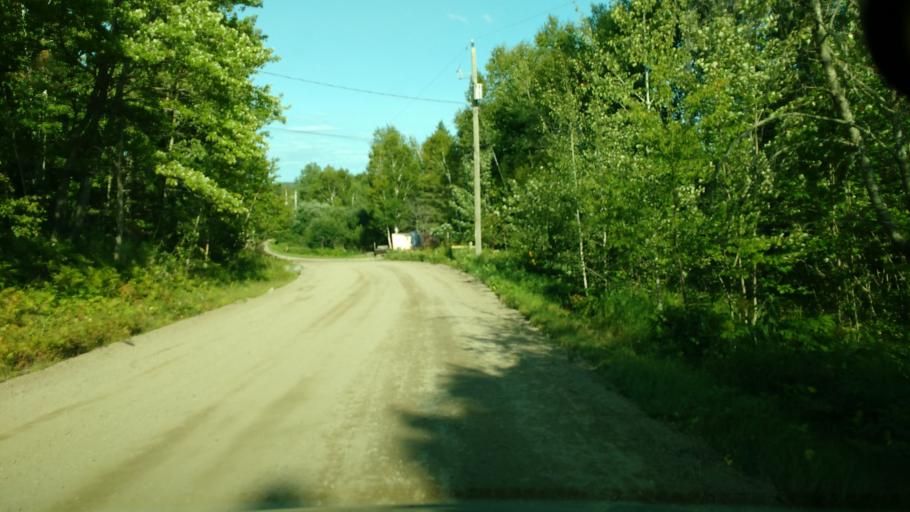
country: CA
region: Ontario
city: Powassan
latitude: 46.1818
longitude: -79.2977
